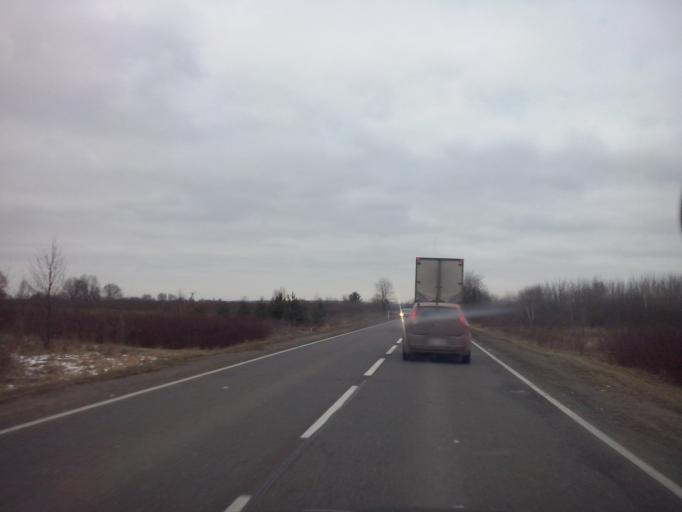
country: PL
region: Subcarpathian Voivodeship
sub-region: Powiat nizanski
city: Rudnik nad Sanem
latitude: 50.4622
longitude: 22.2429
